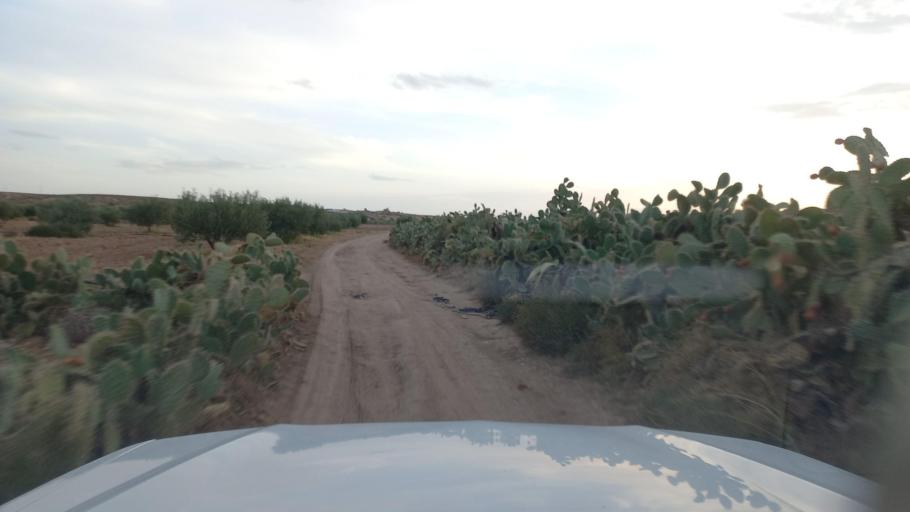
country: TN
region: Al Qasrayn
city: Sbiba
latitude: 35.4128
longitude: 9.0837
